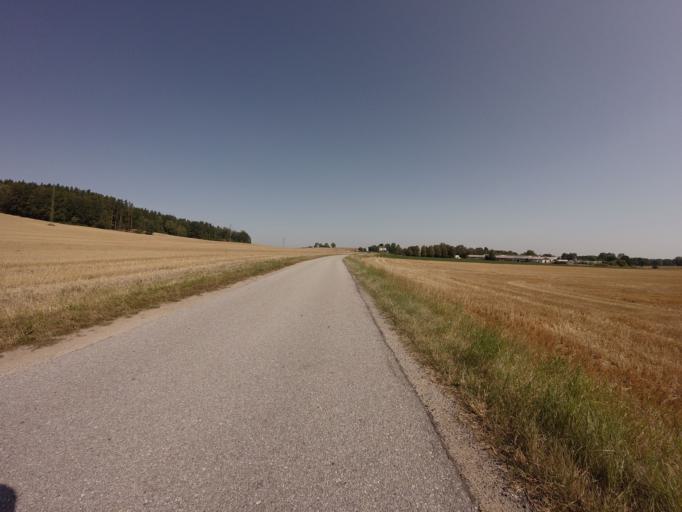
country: CZ
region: Jihocesky
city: Kamenny Ujezd
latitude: 48.8697
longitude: 14.3769
